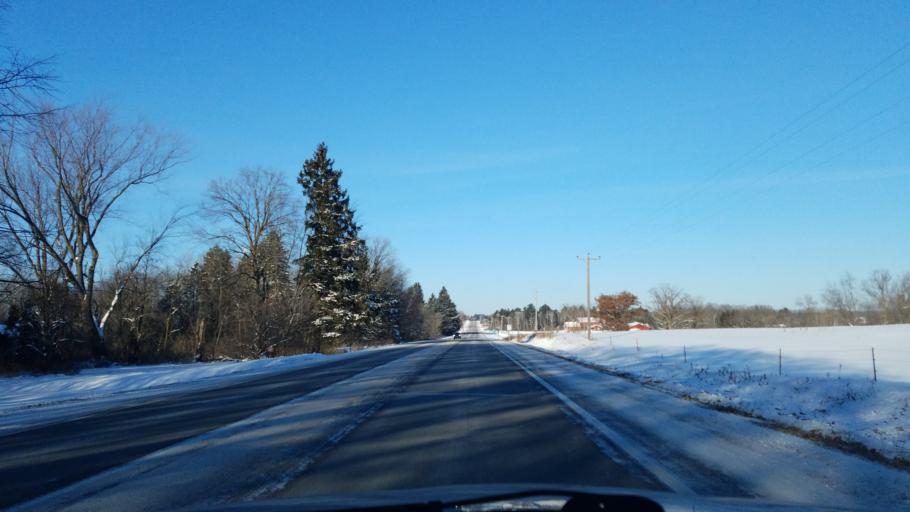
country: US
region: Wisconsin
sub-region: Barron County
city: Cumberland
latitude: 45.5044
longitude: -92.0524
